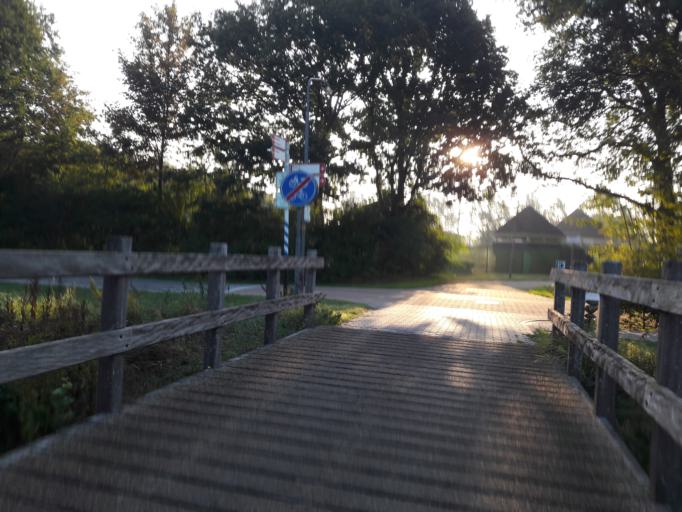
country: NL
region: Drenthe
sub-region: Gemeente Borger-Odoorn
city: Borger
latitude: 52.9242
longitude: 6.8029
